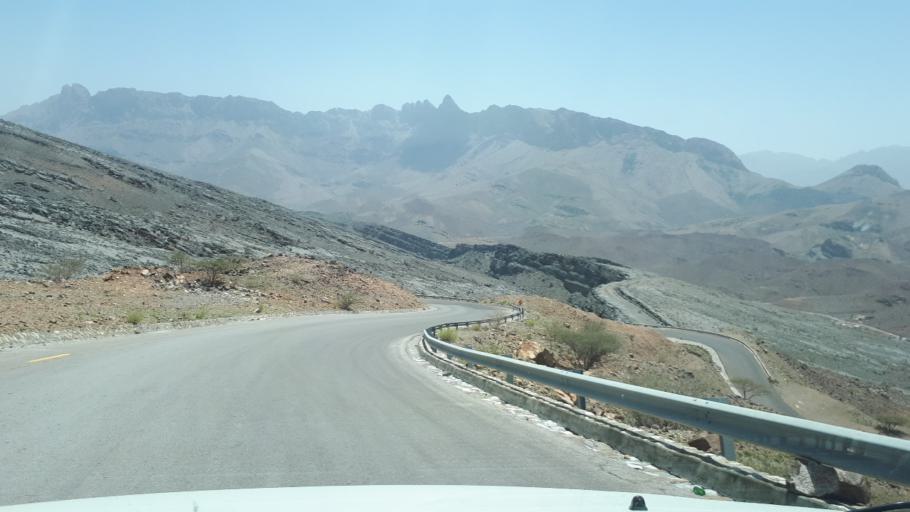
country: OM
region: Muhafazat ad Dakhiliyah
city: Bahla'
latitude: 23.2055
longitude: 57.1457
